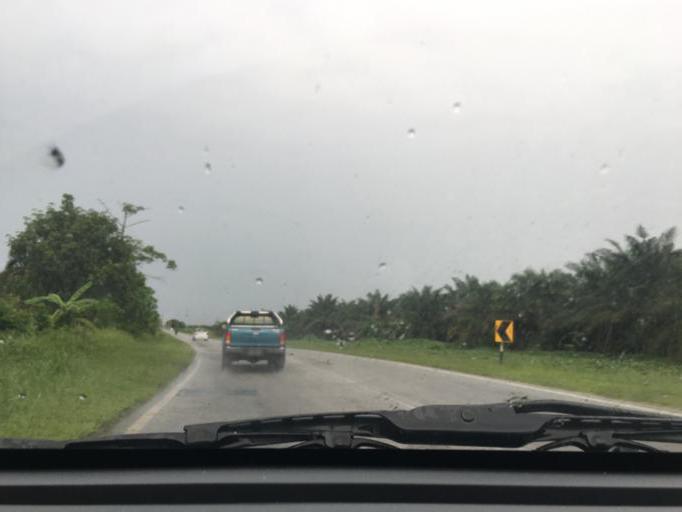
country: MY
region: Kedah
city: Sungai Petani
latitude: 5.6021
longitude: 100.6399
